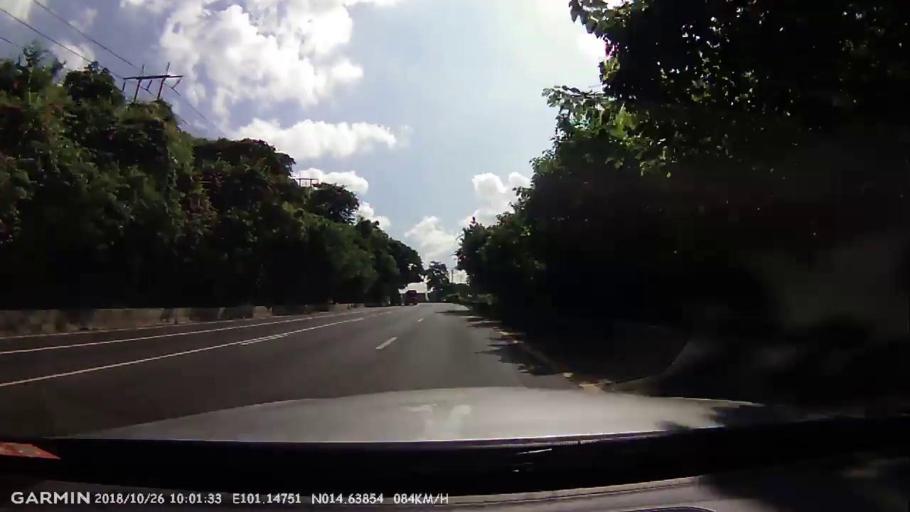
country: TH
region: Sara Buri
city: Muak Lek
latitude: 14.6385
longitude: 101.1476
